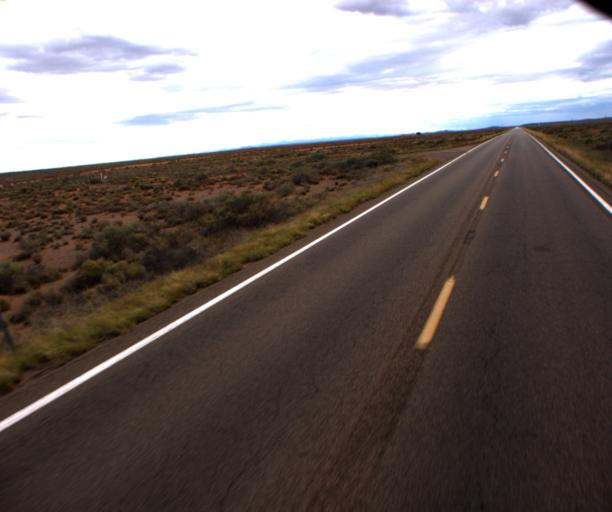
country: US
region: Arizona
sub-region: Navajo County
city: Holbrook
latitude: 34.8138
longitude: -110.1389
